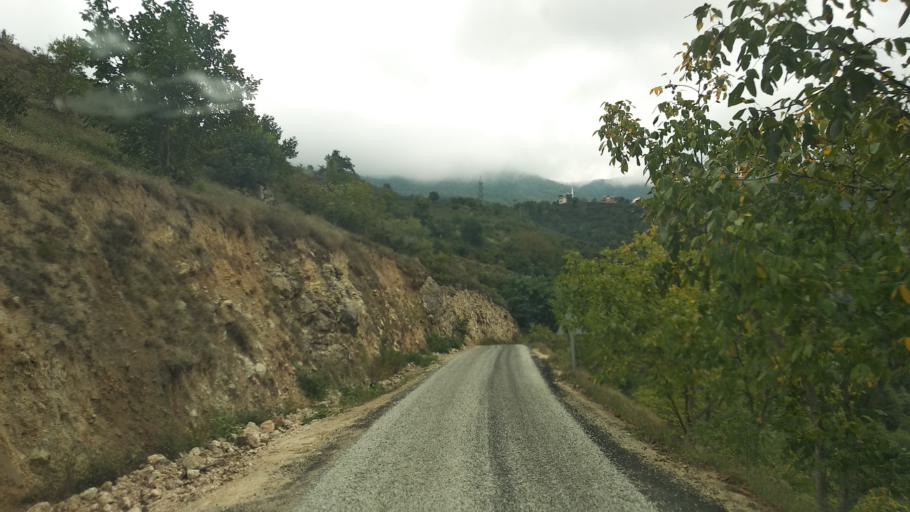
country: TR
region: Giresun
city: Dogankent
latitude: 40.7417
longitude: 38.9907
